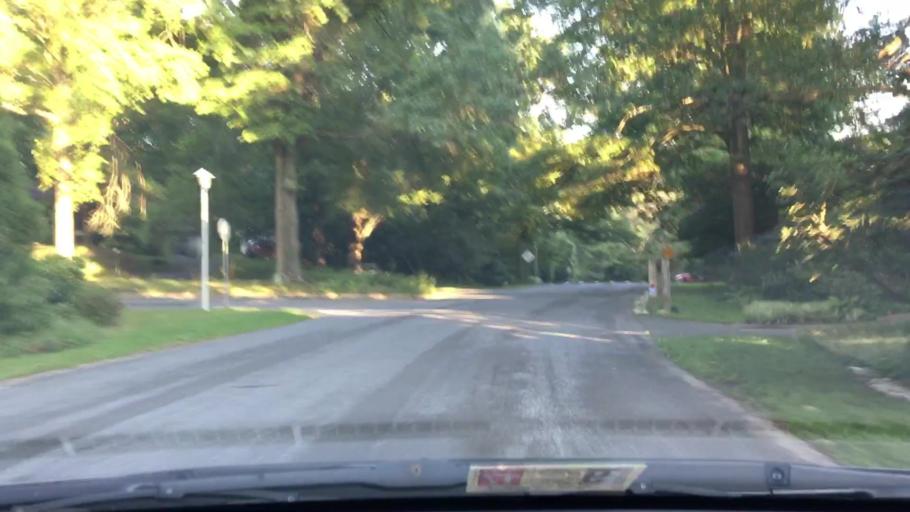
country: US
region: Maryland
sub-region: Montgomery County
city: Cabin John
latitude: 38.9872
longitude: -77.1683
